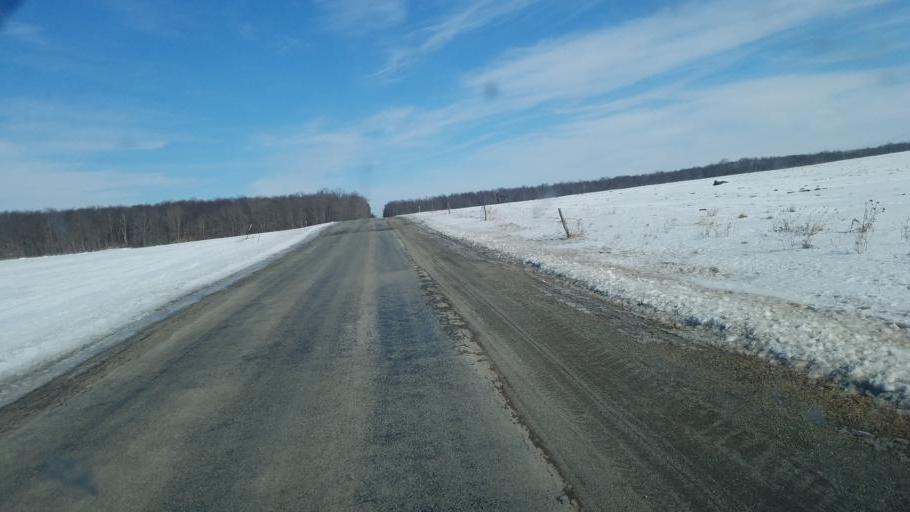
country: US
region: New York
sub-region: Allegany County
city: Andover
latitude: 42.0634
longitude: -77.7720
